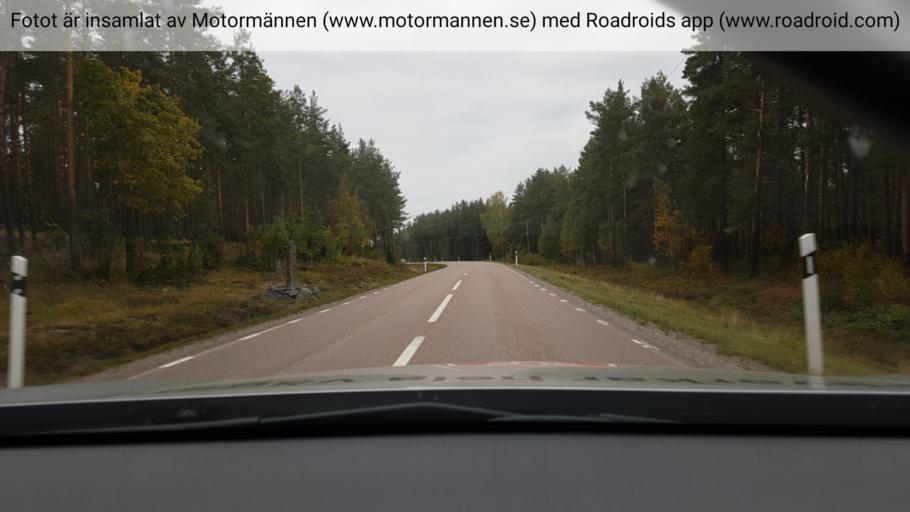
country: SE
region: Gaevleborg
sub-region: Gavle Kommun
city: Hedesunda
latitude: 60.5229
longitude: 16.9433
